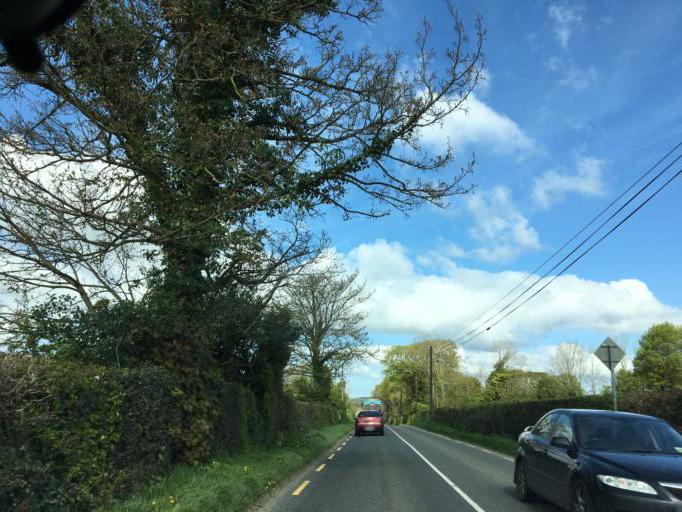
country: IE
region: Leinster
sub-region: Loch Garman
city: New Ross
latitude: 52.4305
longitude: -6.9512
